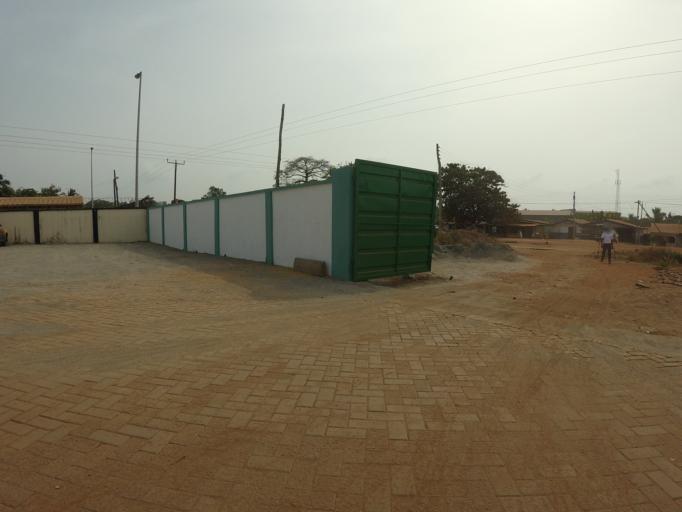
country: GH
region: Volta
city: Ho
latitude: 6.5987
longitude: 0.4468
